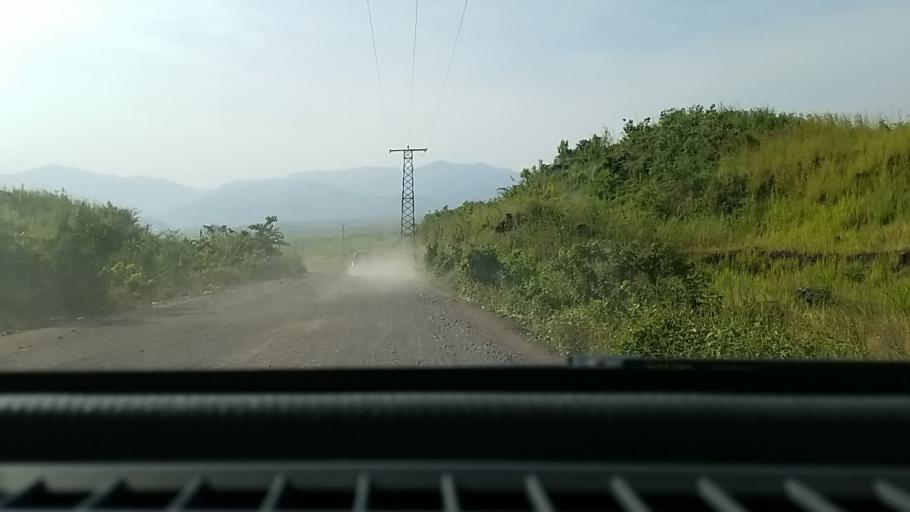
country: CD
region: Nord Kivu
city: Sake
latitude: -1.5912
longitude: 29.0975
